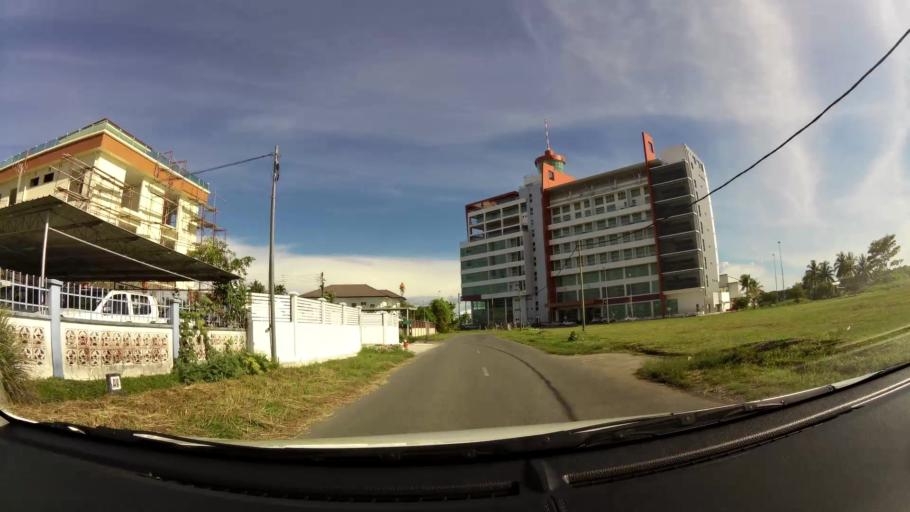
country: BN
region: Belait
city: Kuala Belait
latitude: 4.5797
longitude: 114.1959
